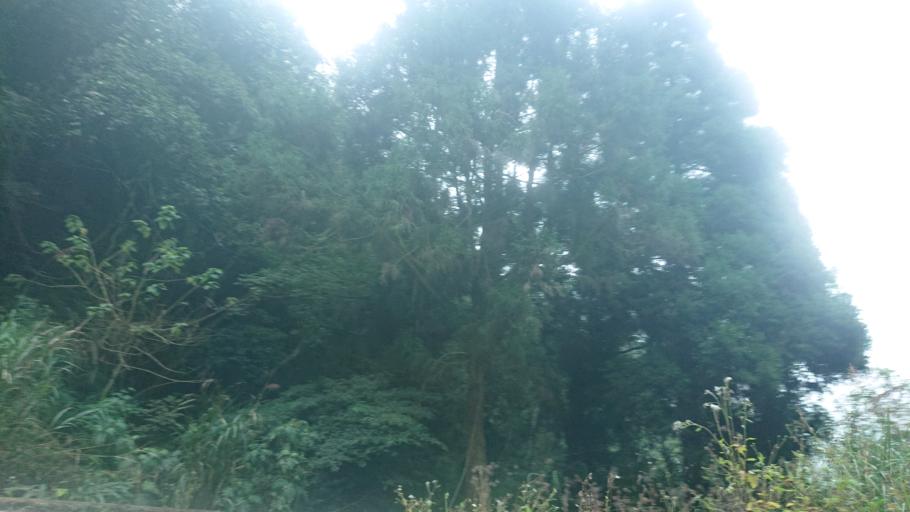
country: TW
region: Taiwan
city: Lugu
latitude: 23.6241
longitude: 120.7183
